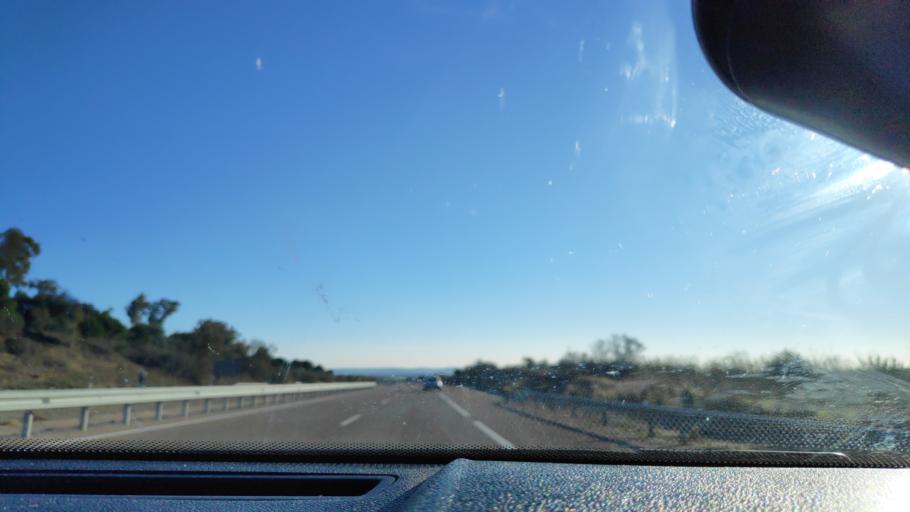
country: ES
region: Andalusia
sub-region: Provincia de Sevilla
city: Guillena
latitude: 37.5605
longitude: -6.1033
